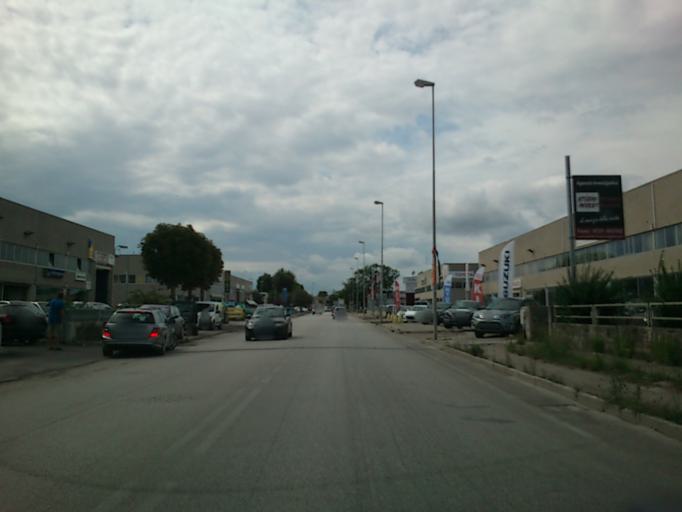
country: IT
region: The Marches
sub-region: Provincia di Pesaro e Urbino
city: Fano
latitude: 43.8305
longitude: 13.0420
